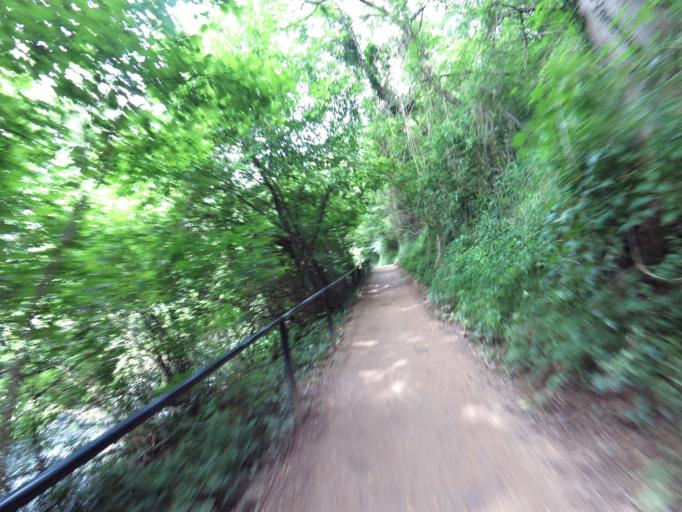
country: NL
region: Limburg
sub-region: Valkenburg aan de Geul
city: Schin op Geul
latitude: 50.8581
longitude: 5.8576
